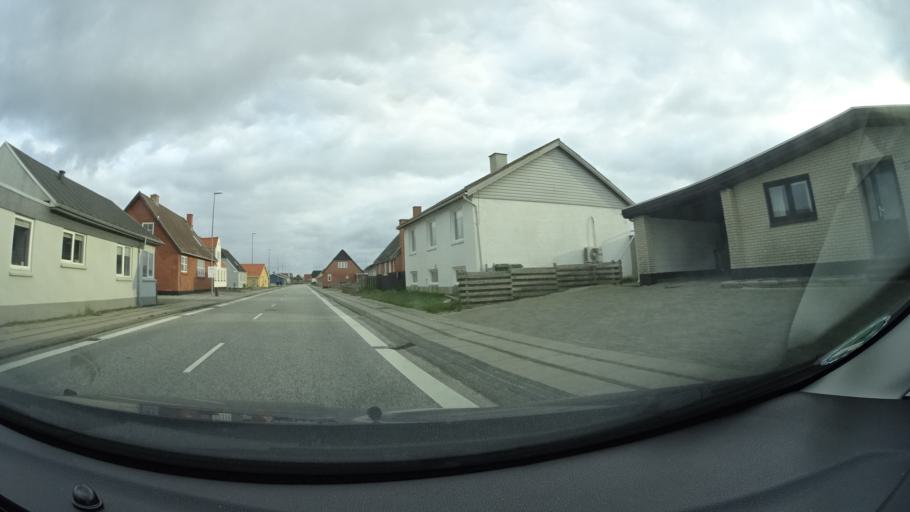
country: DK
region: Central Jutland
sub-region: Holstebro Kommune
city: Ulfborg
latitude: 56.3764
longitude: 8.1202
